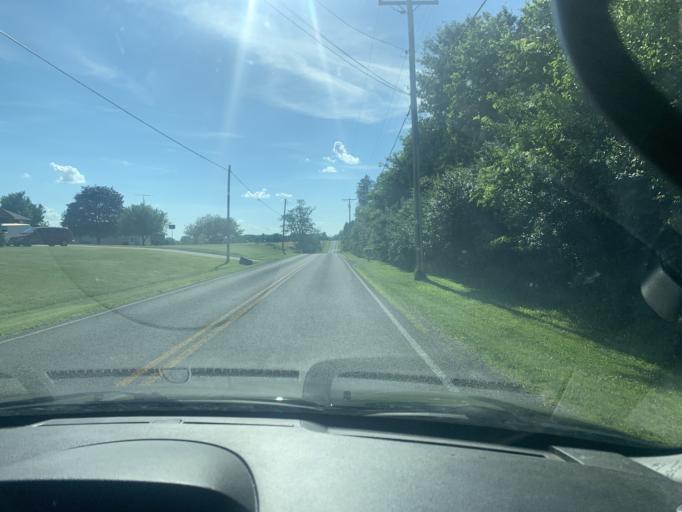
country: US
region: Ohio
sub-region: Logan County
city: Bellefontaine
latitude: 40.3494
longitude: -83.8051
